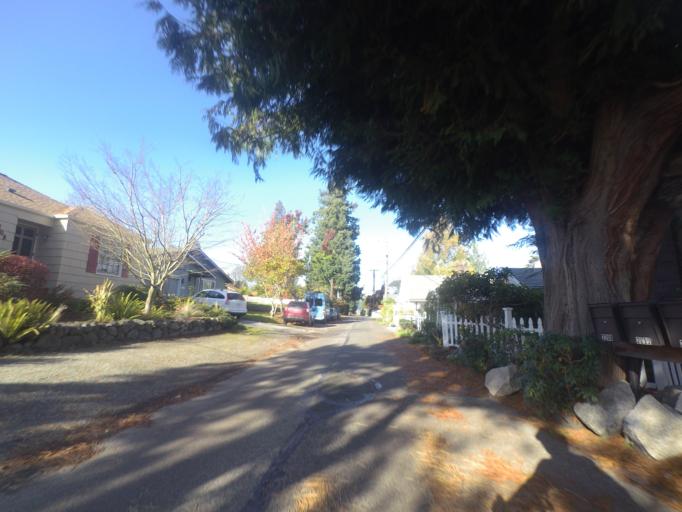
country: US
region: Washington
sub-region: Pierce County
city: University Place
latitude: 47.2400
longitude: -122.5620
